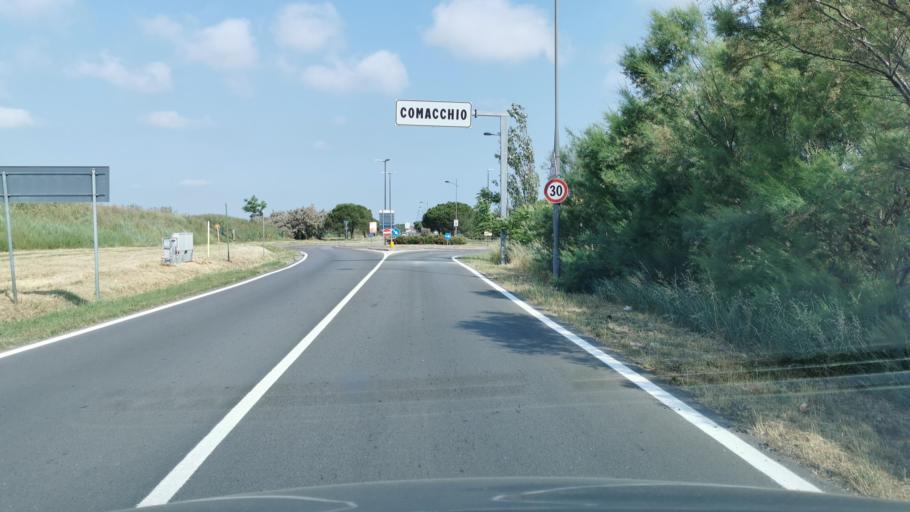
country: IT
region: Emilia-Romagna
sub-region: Provincia di Ferrara
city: Comacchio
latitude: 44.6839
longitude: 12.1968
